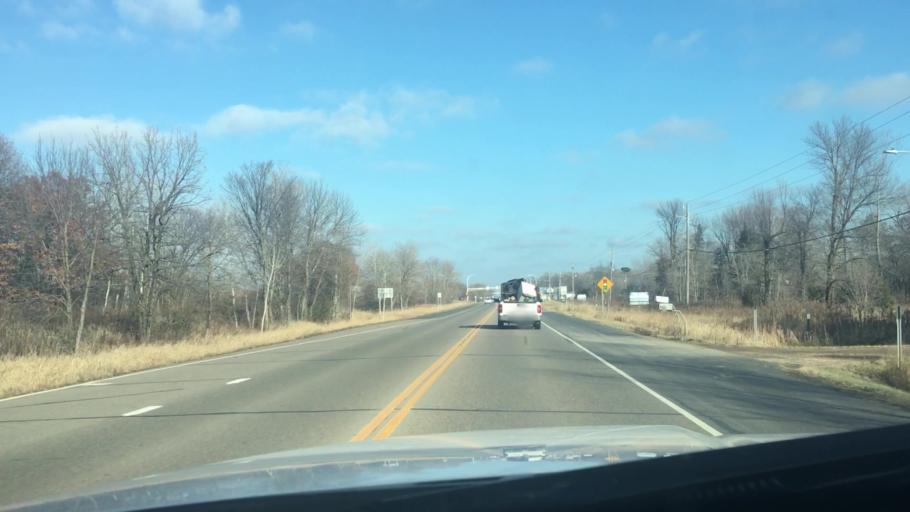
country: US
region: Minnesota
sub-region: Washington County
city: Hugo
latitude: 45.1490
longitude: -92.9964
